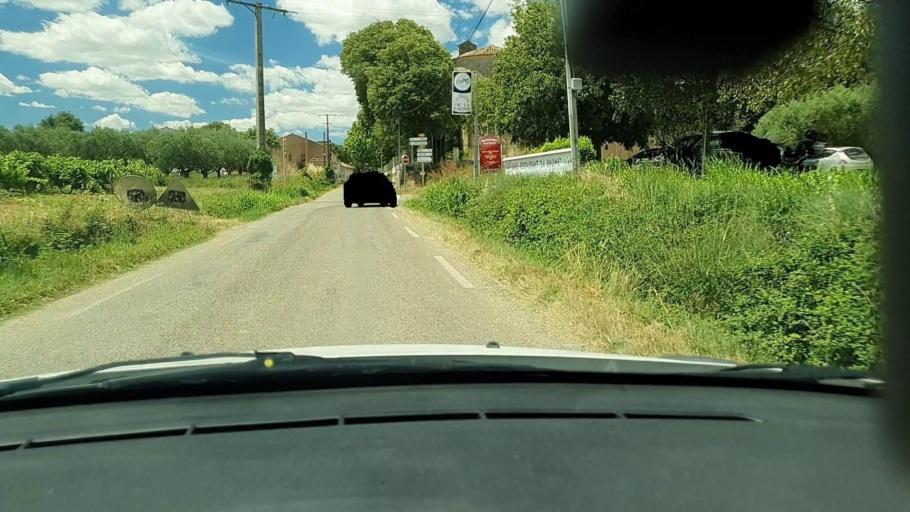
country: FR
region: Languedoc-Roussillon
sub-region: Departement du Gard
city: Poulx
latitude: 43.9536
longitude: 4.4268
